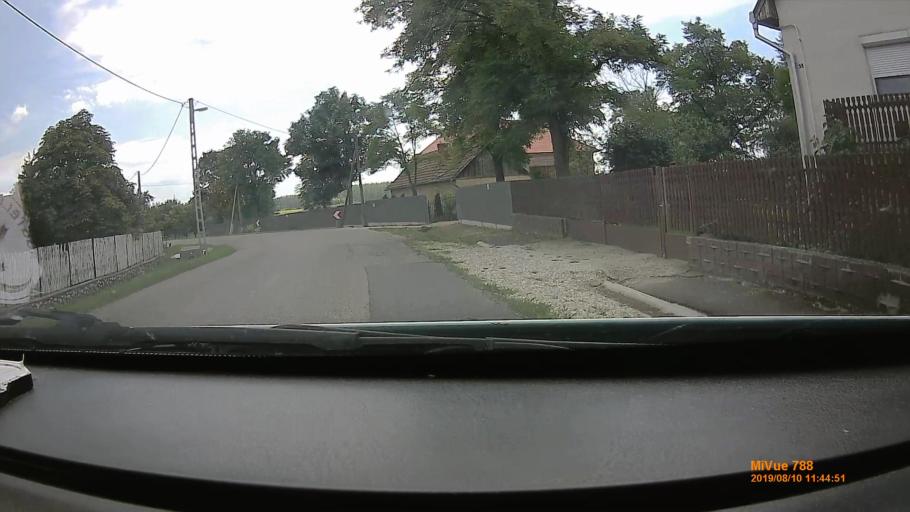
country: HU
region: Borsod-Abauj-Zemplen
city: Szentistvan
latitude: 47.7194
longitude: 20.6234
